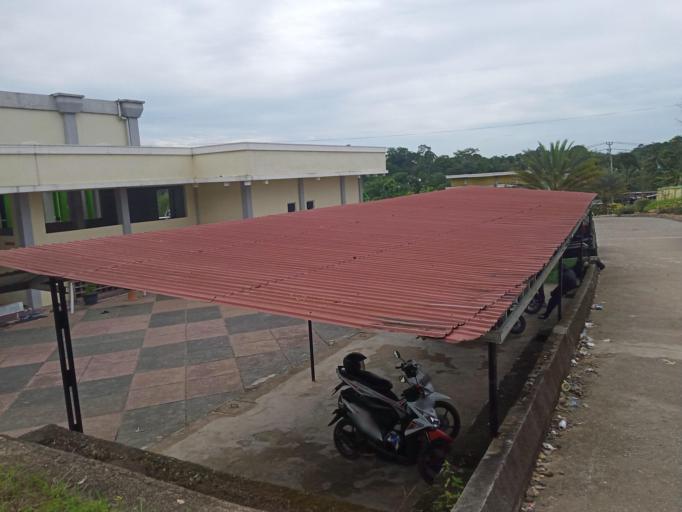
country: ID
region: Jambi
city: Bangko
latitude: -2.0762
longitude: 102.2877
